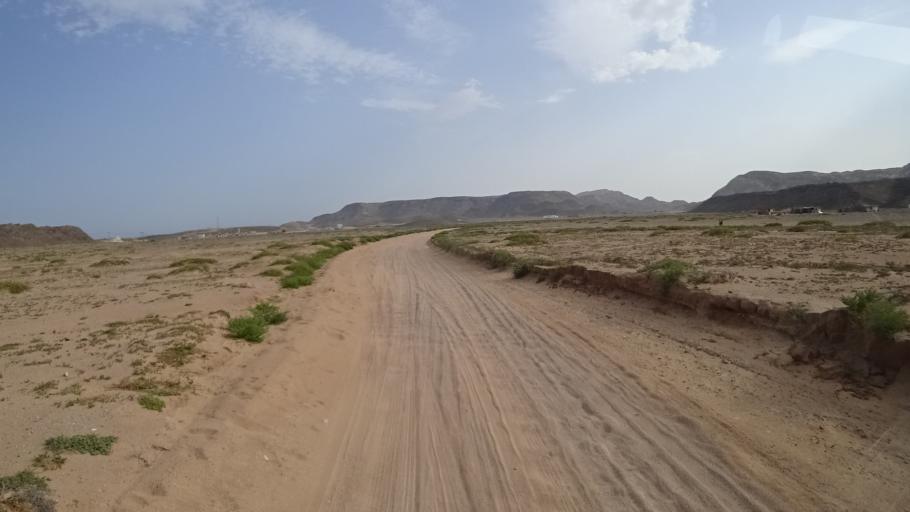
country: OM
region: Ash Sharqiyah
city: Sur
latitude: 22.4477
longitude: 59.8254
